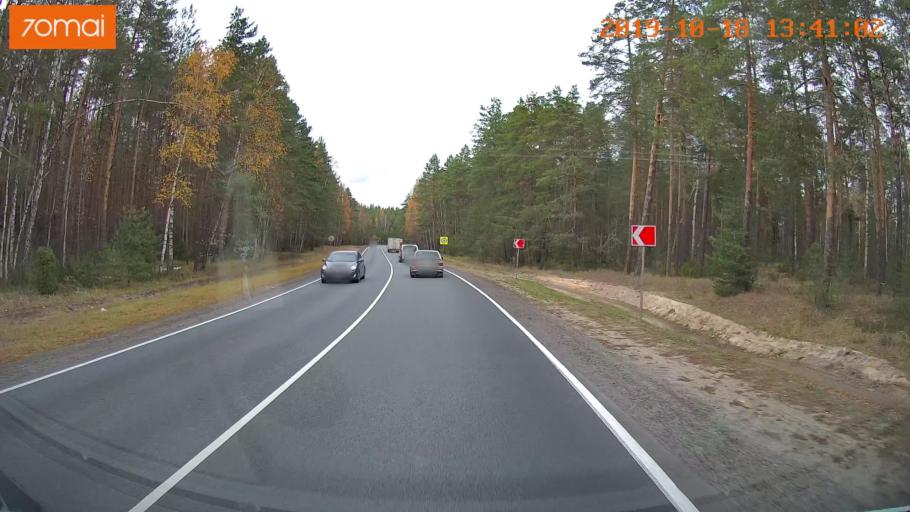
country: RU
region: Rjazan
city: Solotcha
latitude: 54.9166
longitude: 39.9976
